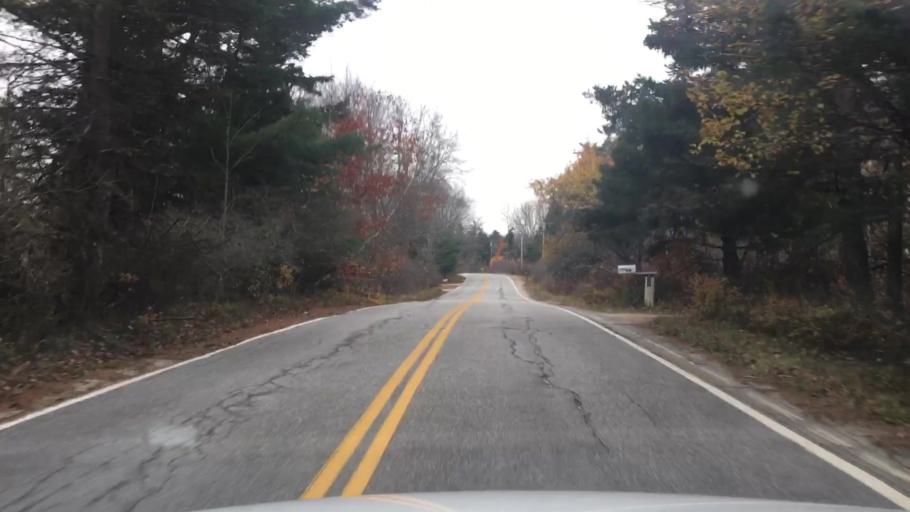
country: US
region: Maine
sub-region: Hancock County
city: Sedgwick
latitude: 44.2905
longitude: -68.5550
